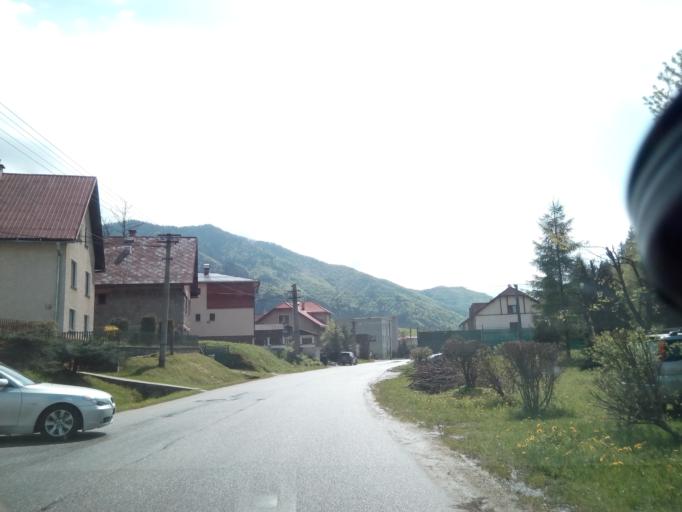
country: SK
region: Zilinsky
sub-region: Okres Zilina
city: Terchova
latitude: 49.2610
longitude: 19.0320
